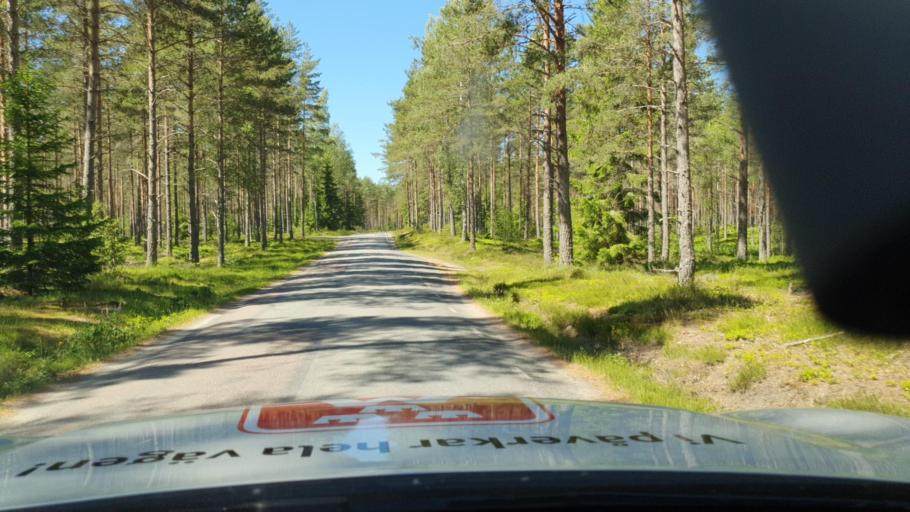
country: SE
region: Joenkoeping
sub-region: Habo Kommun
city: Habo
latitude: 57.8914
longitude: 13.9891
